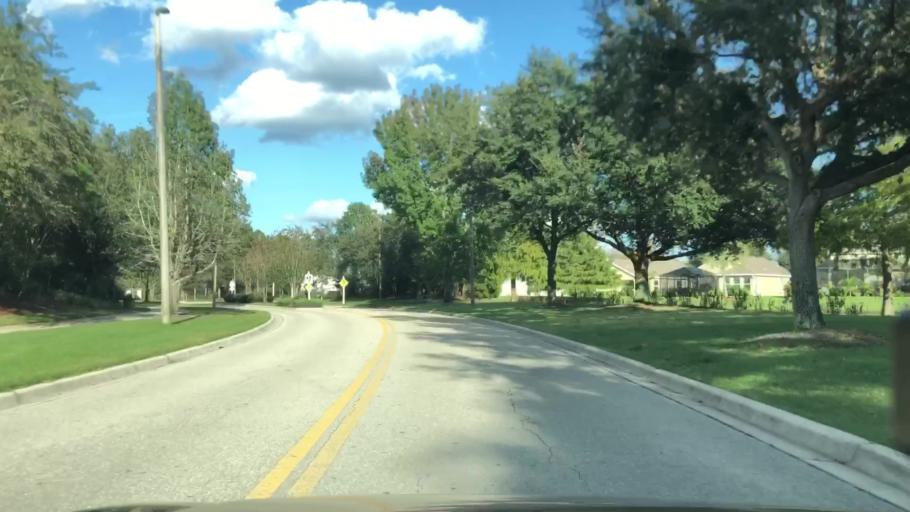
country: US
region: Florida
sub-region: Sarasota County
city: The Meadows
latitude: 27.4284
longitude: -82.4050
